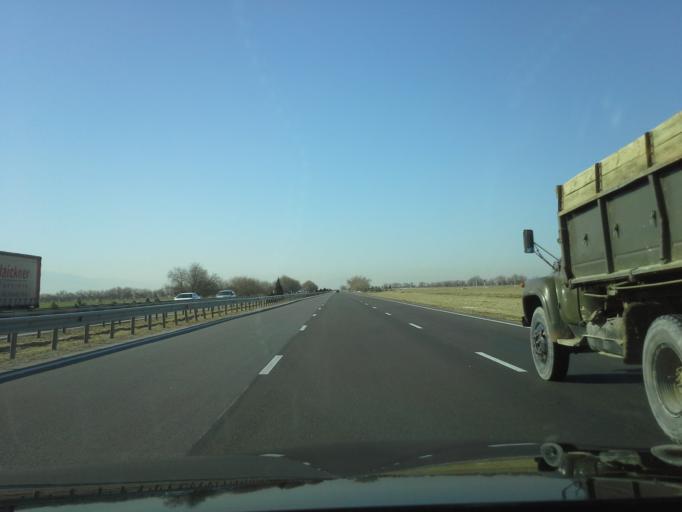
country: TM
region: Ahal
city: Annau
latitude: 37.8992
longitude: 58.5831
